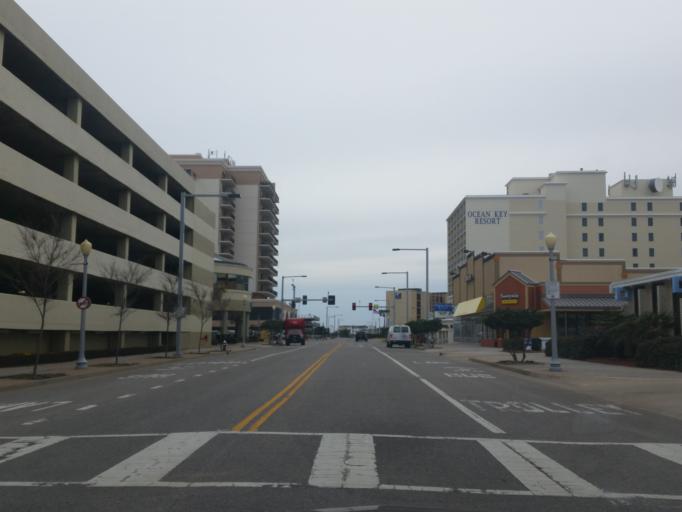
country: US
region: Virginia
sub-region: City of Virginia Beach
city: Virginia Beach
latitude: 36.8347
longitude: -75.9715
